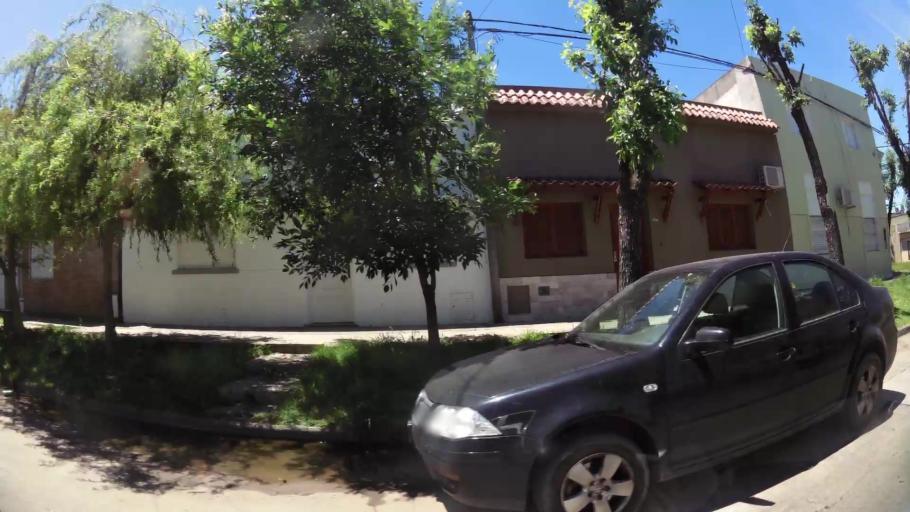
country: AR
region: Santa Fe
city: Santa Fe de la Vera Cruz
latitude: -31.6259
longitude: -60.7116
